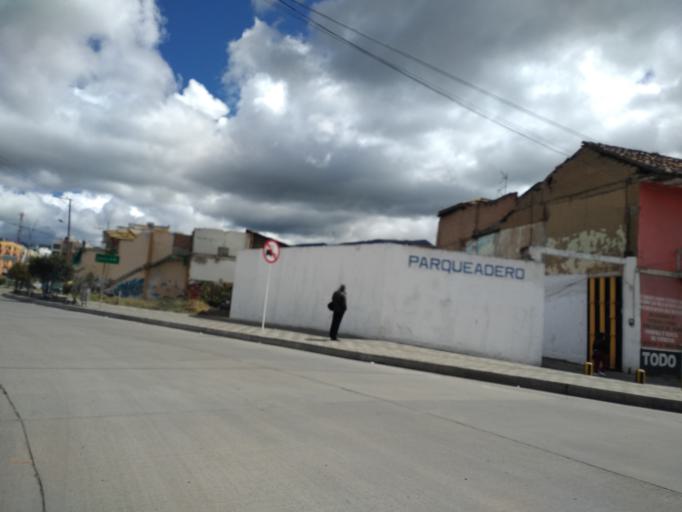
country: CO
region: Narino
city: Pasto
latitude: 1.2104
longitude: -77.2738
